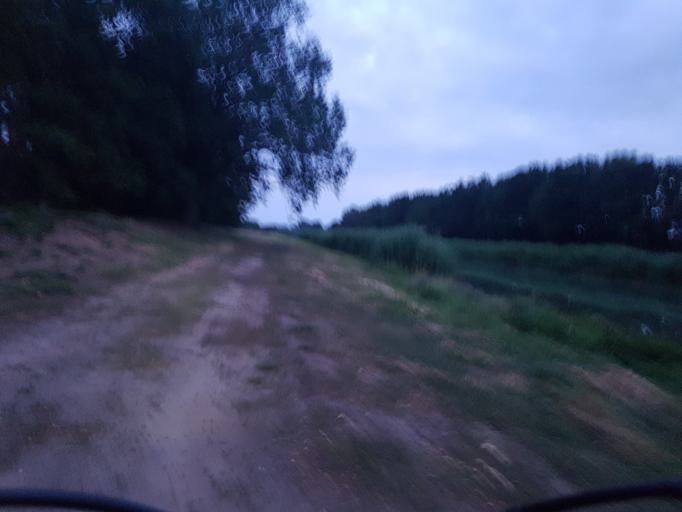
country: DE
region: Brandenburg
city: Schilda
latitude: 51.5675
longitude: 13.3565
